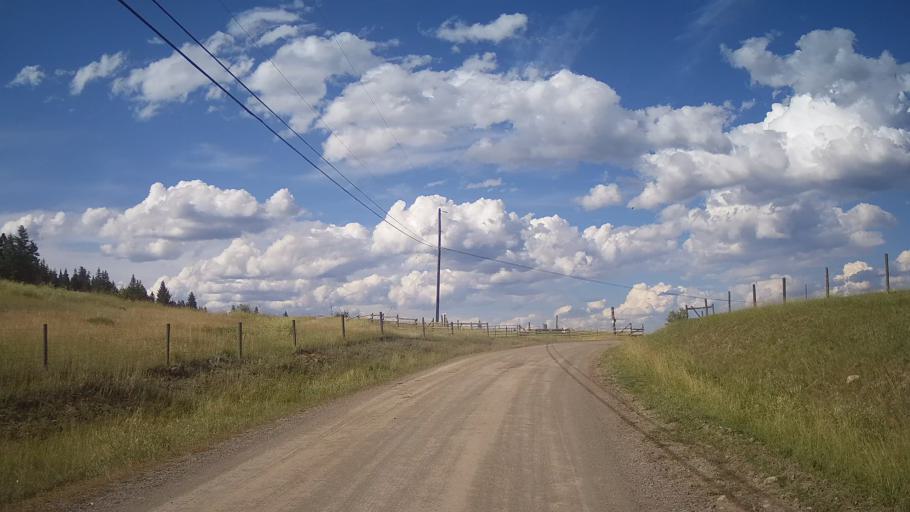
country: CA
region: British Columbia
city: Lillooet
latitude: 51.3071
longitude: -121.9877
